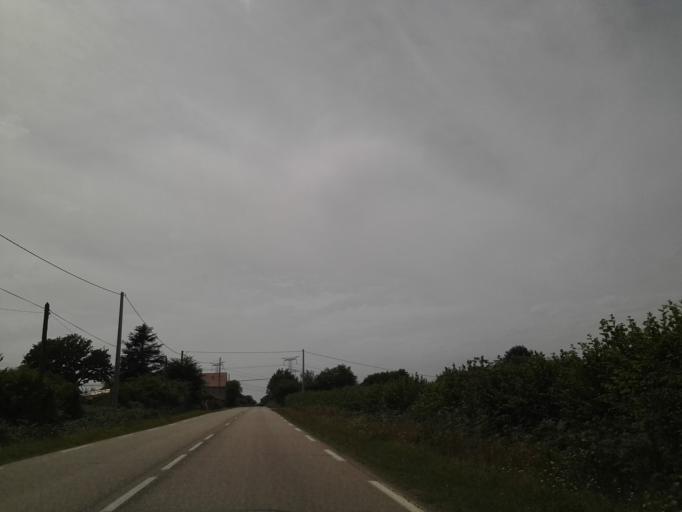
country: FR
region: Lower Normandy
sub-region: Departement de la Manche
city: Sottevast
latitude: 49.4867
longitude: -1.5815
